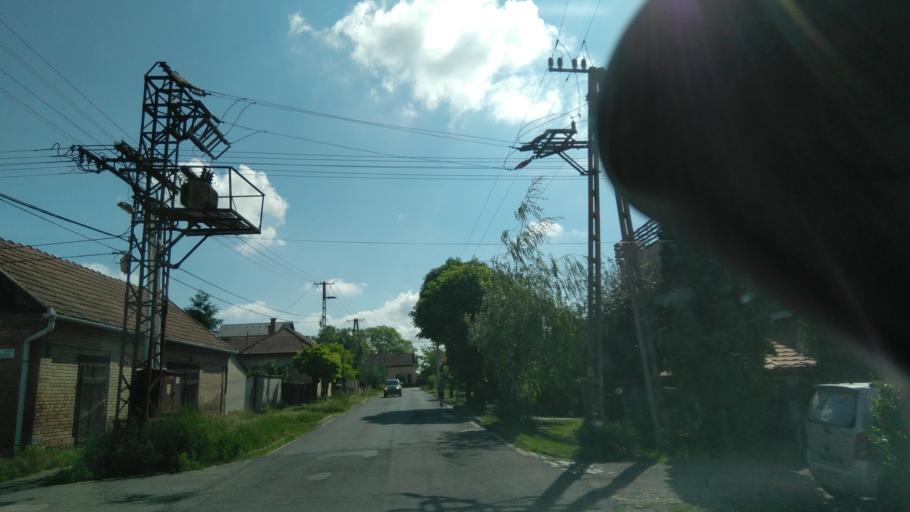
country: HU
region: Bekes
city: Bekes
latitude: 46.7766
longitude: 21.1324
